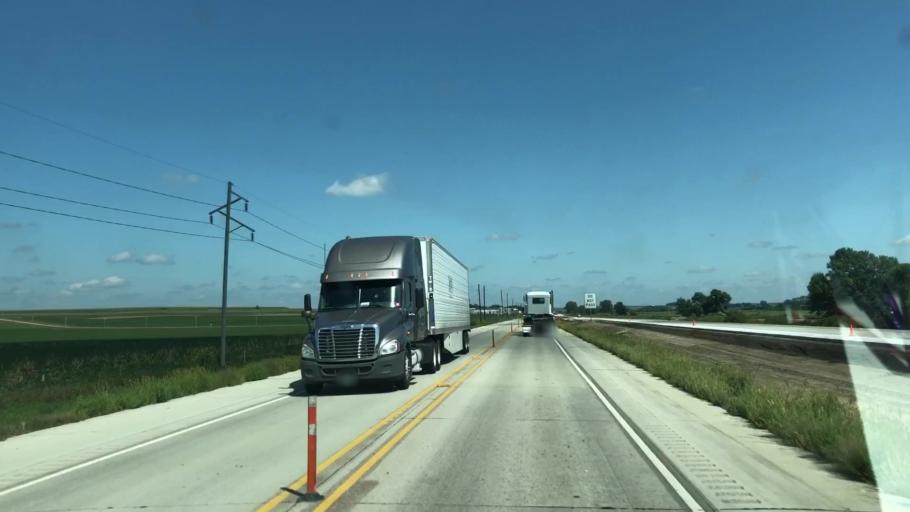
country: US
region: Iowa
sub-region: Plymouth County
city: Le Mars
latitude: 42.7272
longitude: -96.2366
